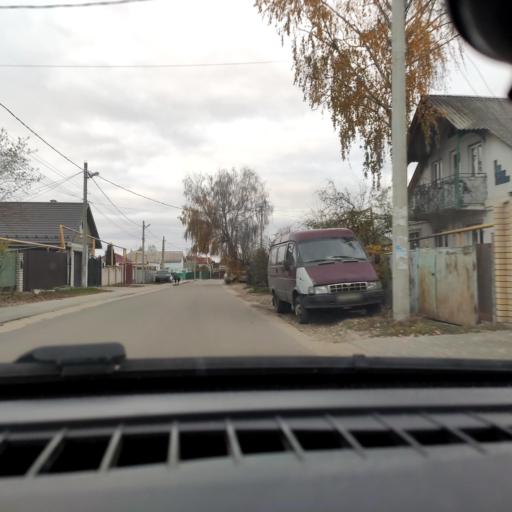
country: RU
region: Voronezj
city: Podgornoye
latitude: 51.7318
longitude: 39.1585
